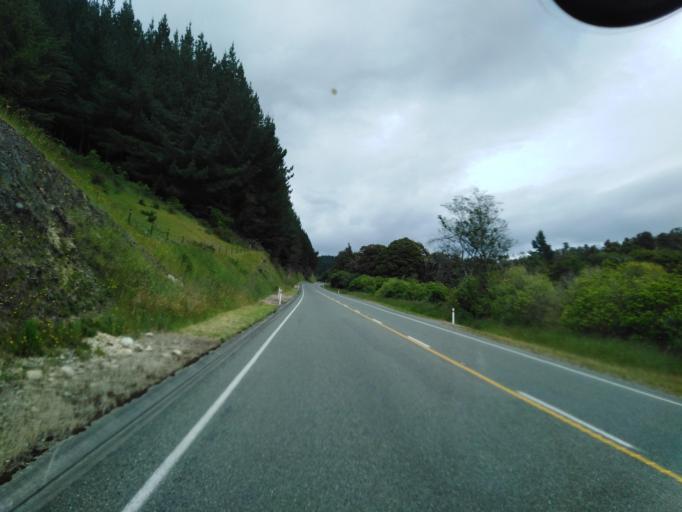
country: NZ
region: Tasman
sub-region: Tasman District
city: Wakefield
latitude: -41.4735
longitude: 172.9378
